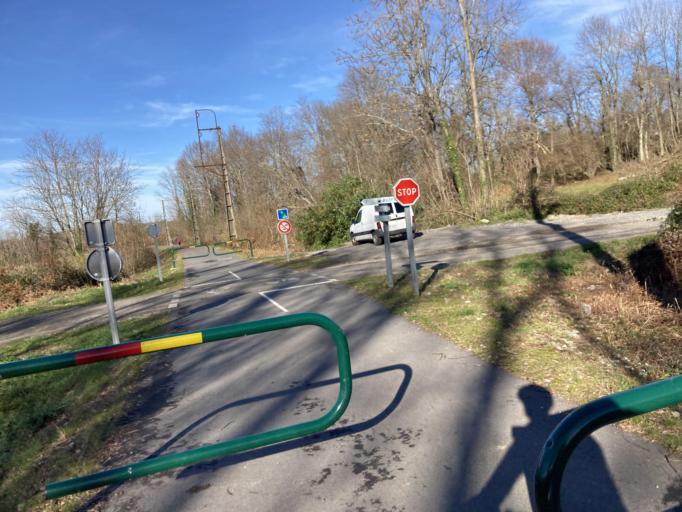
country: FR
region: Aquitaine
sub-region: Departement des Pyrenees-Atlantiques
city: Arudy
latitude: 43.1380
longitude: -0.4476
